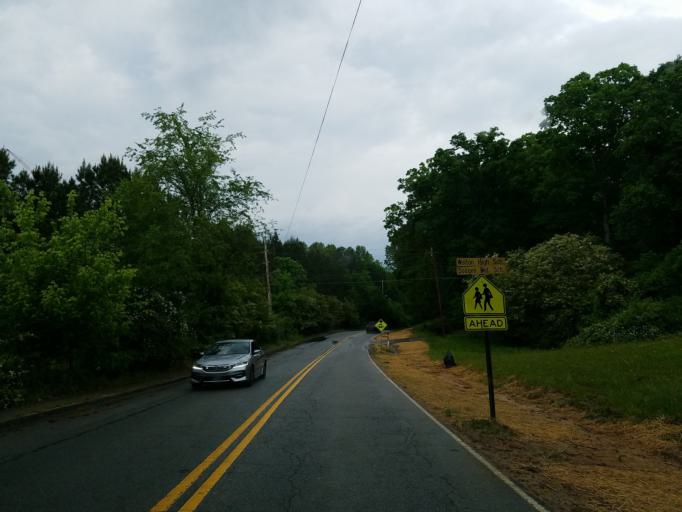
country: US
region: Georgia
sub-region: Fulton County
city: Roswell
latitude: 33.9859
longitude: -84.4399
